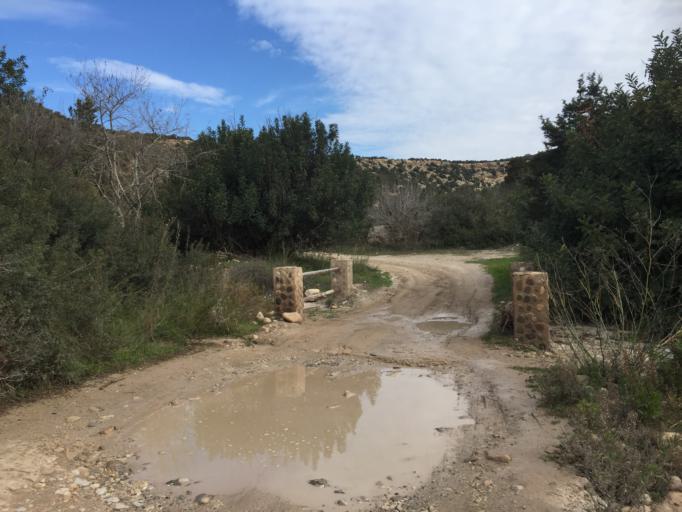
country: CY
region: Pafos
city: Pegeia
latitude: 34.9199
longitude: 32.3374
